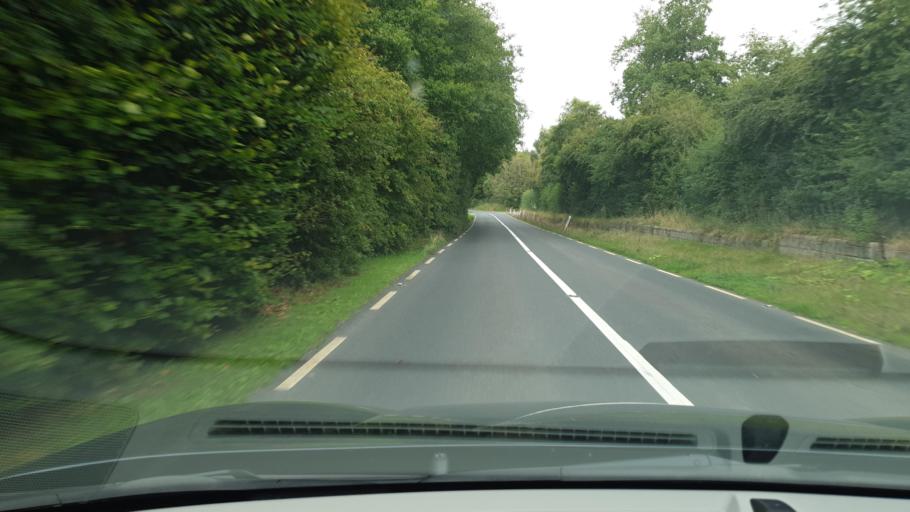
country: IE
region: Leinster
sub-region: Kildare
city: Naas
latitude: 53.2279
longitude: -6.7025
